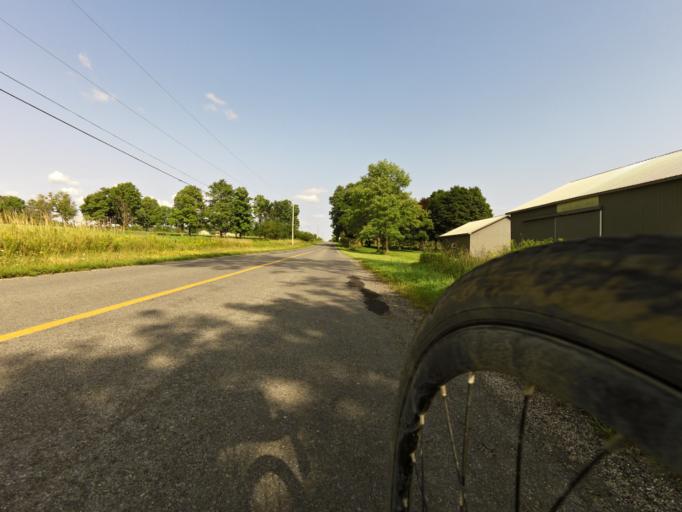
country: CA
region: Ontario
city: Kingston
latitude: 44.3686
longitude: -76.6093
